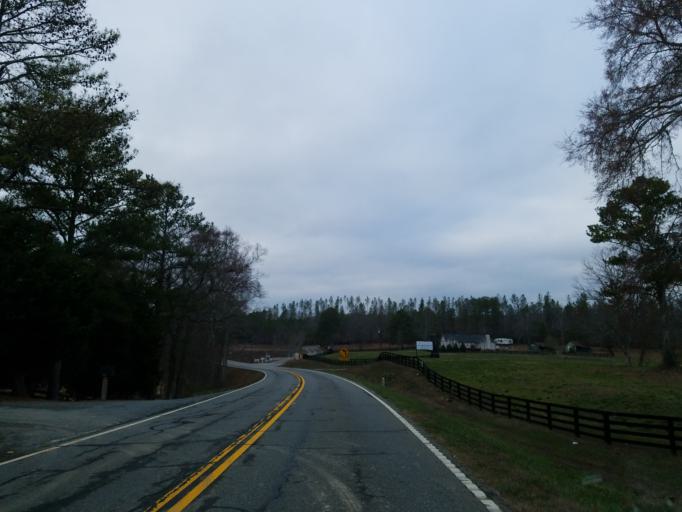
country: US
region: Georgia
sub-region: Bartow County
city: Rydal
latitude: 34.3448
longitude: -84.5790
